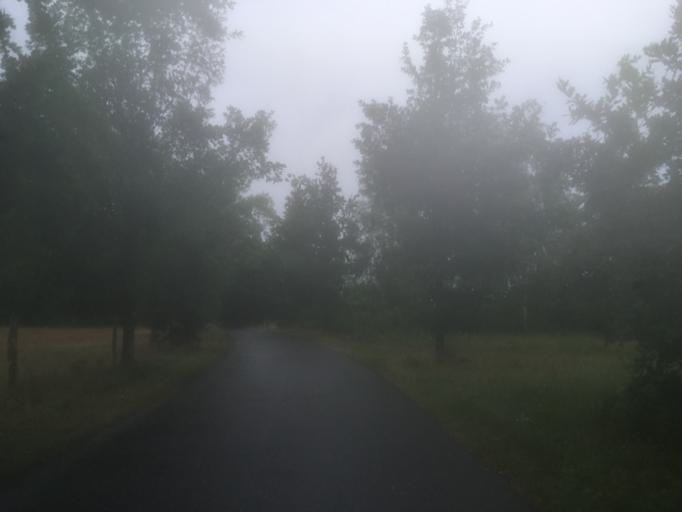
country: DE
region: Brandenburg
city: Zehdenick
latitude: 53.0126
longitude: 13.3148
